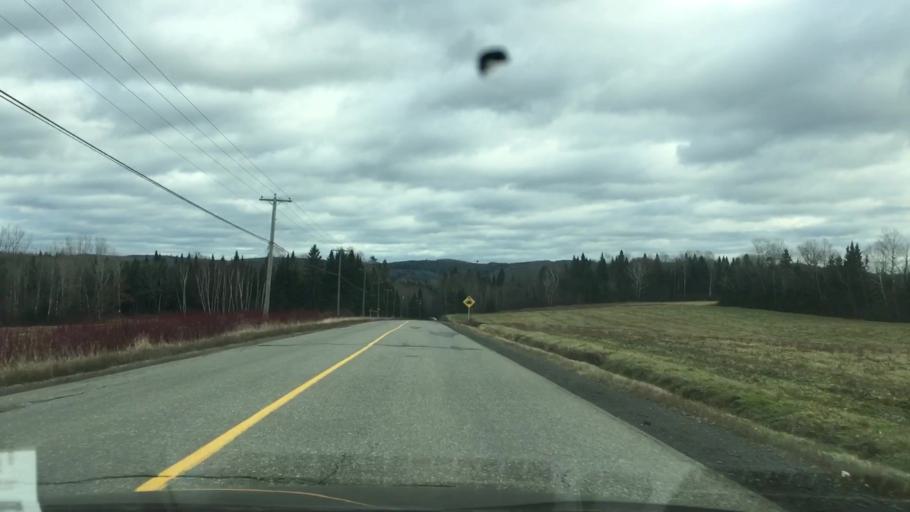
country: US
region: Maine
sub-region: Aroostook County
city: Fort Fairfield
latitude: 46.7501
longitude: -67.7342
